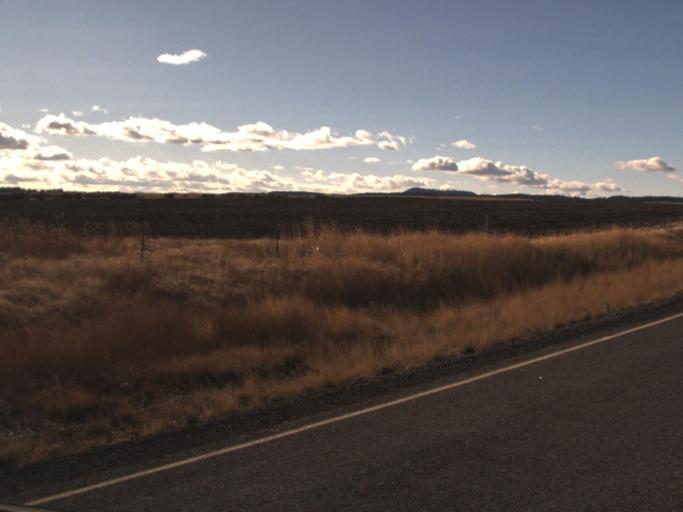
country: US
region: Washington
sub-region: Asotin County
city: Asotin
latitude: 46.1614
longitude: -117.1028
